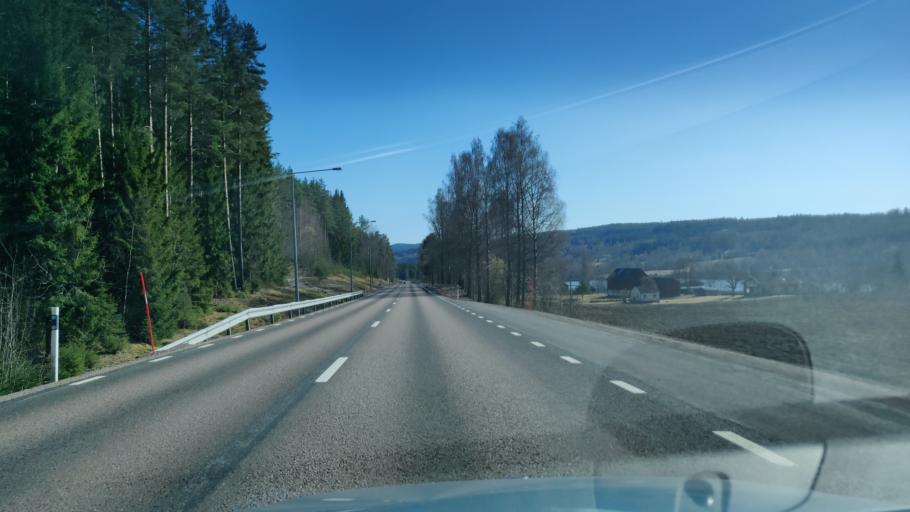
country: SE
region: Vaermland
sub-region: Hagfors Kommun
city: Hagfors
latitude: 59.9359
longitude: 13.6770
